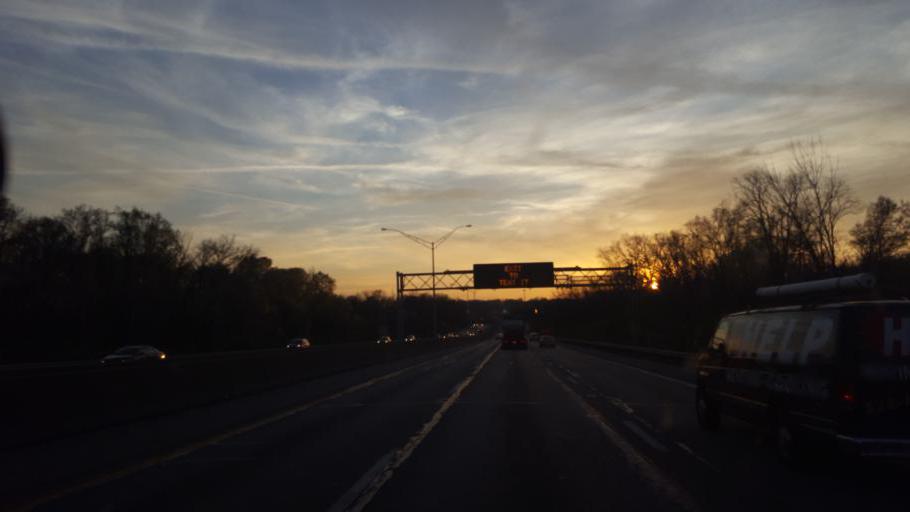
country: US
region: Ohio
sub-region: Hamilton County
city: Silverton
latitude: 39.1708
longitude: -84.4100
